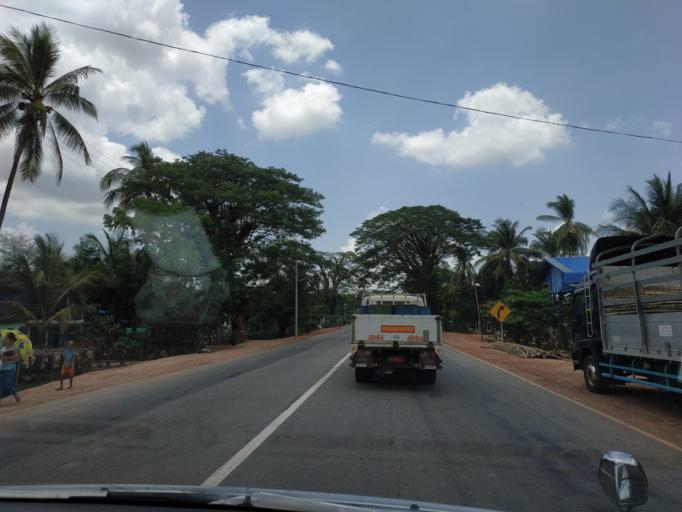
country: MM
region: Bago
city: Bago
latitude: 17.4669
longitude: 96.5826
